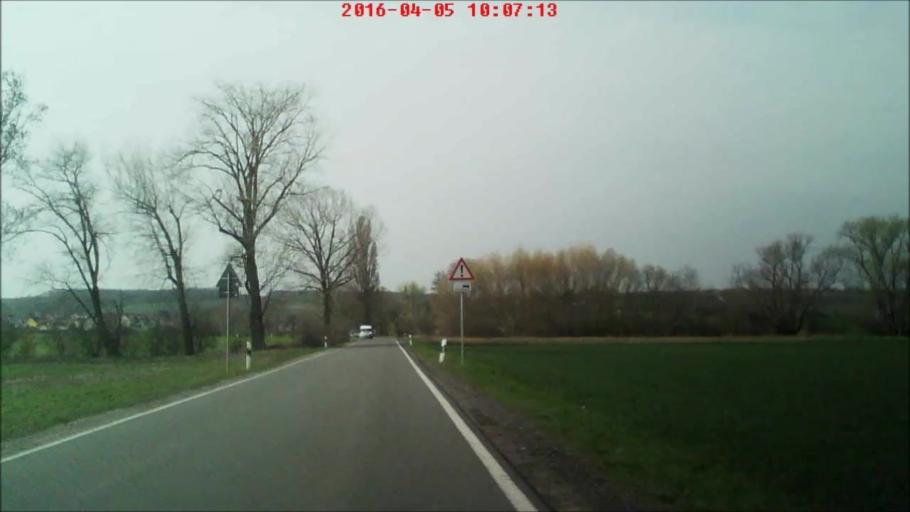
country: DE
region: Thuringia
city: Elxleben
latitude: 51.0294
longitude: 10.9602
